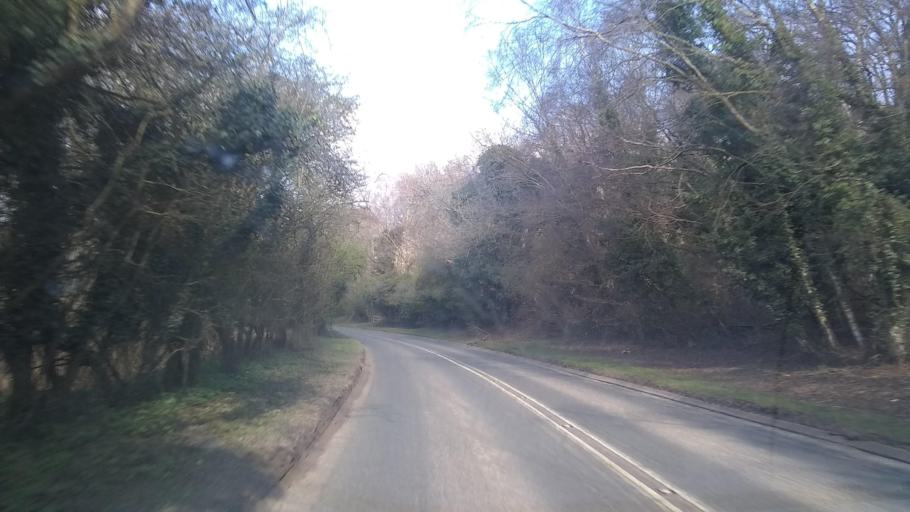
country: GB
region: England
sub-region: Worcestershire
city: Stourport-on-Severn
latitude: 52.3633
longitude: -2.2499
